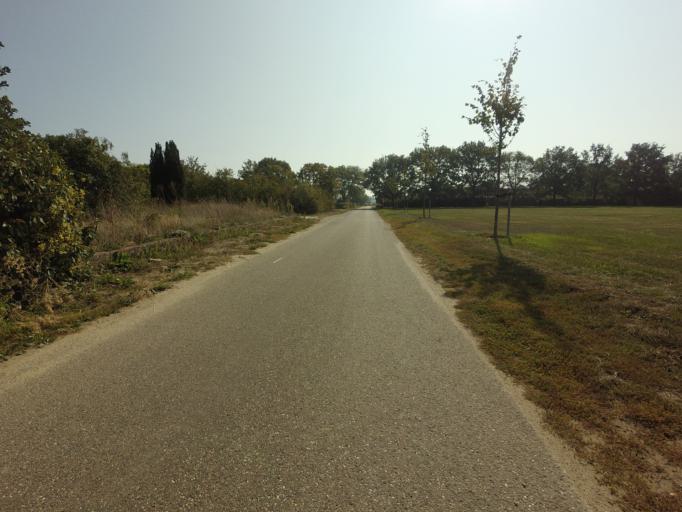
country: NL
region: Limburg
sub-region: Gemeente Roermond
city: Leeuwen
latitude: 51.2509
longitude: 6.0020
